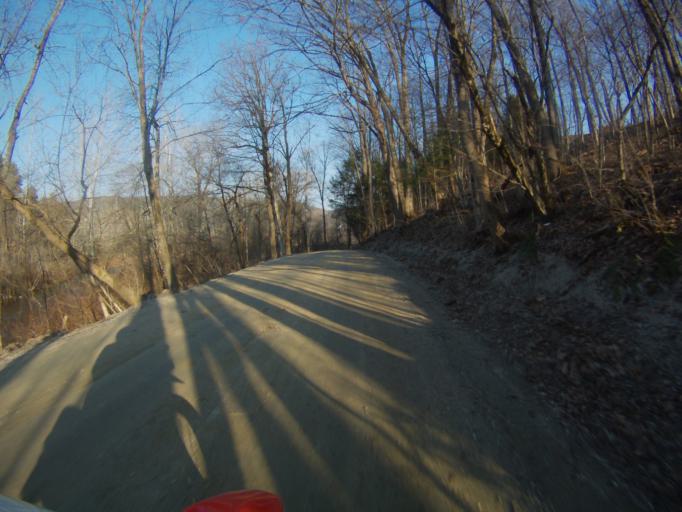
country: US
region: Vermont
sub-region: Addison County
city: Bristol
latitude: 44.0924
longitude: -73.1052
